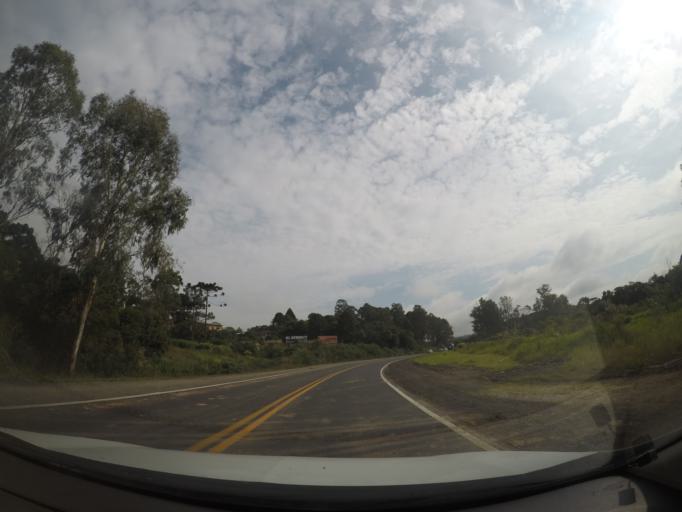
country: BR
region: Parana
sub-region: Colombo
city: Colombo
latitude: -25.3412
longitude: -49.2404
